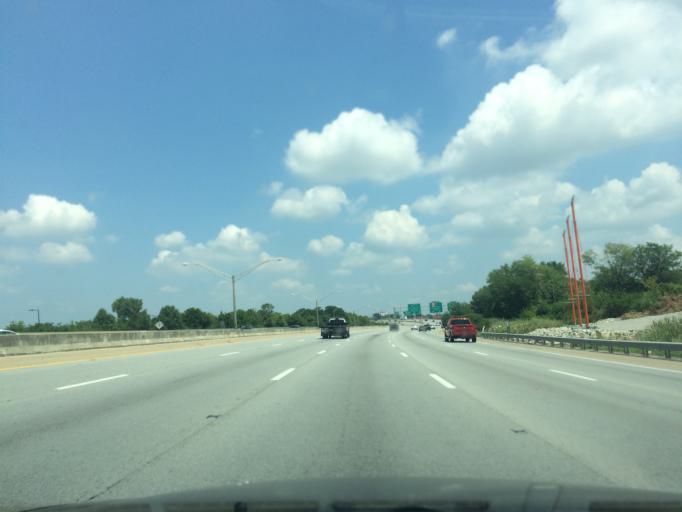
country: US
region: Kentucky
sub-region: Jefferson County
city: Audubon Park
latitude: 38.1712
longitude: -85.7204
